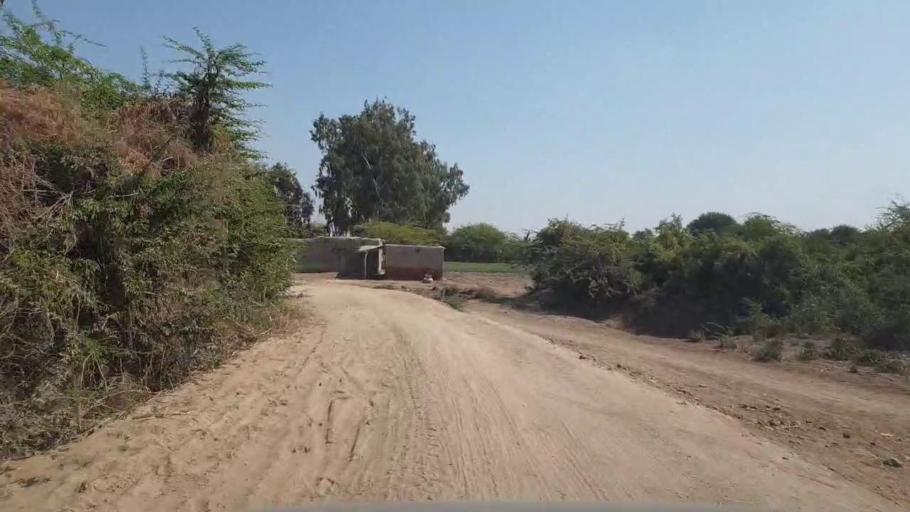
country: PK
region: Sindh
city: Digri
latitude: 25.0911
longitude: 69.2328
